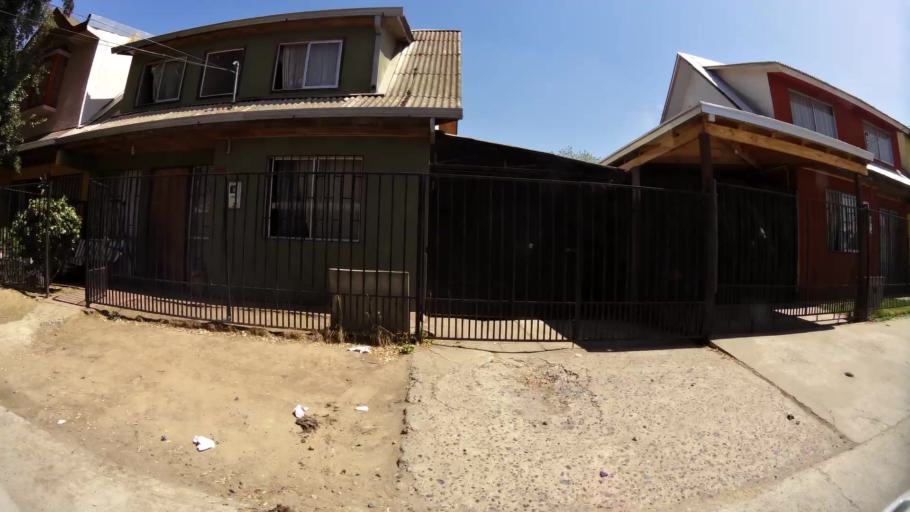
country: CL
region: Maule
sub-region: Provincia de Talca
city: Talca
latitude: -35.4238
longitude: -71.6283
